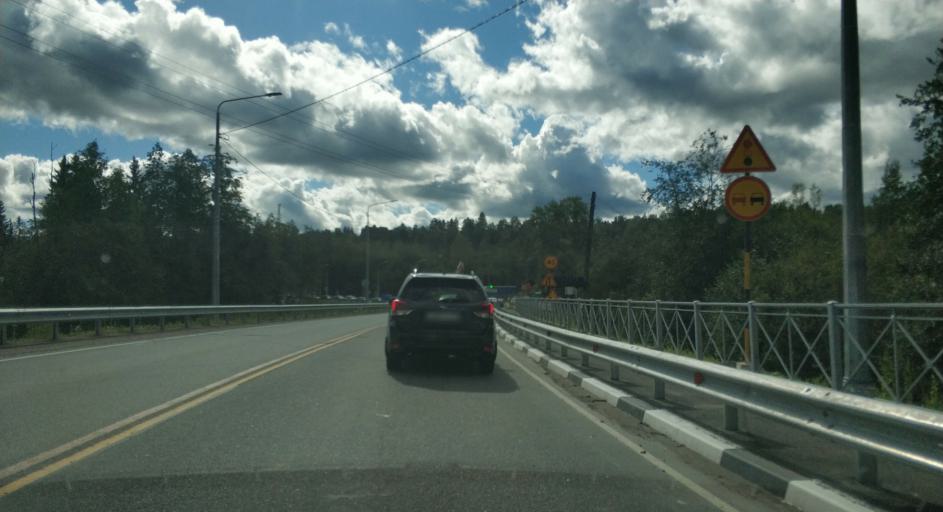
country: RU
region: Republic of Karelia
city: Ruskeala
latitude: 61.9388
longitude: 30.5918
